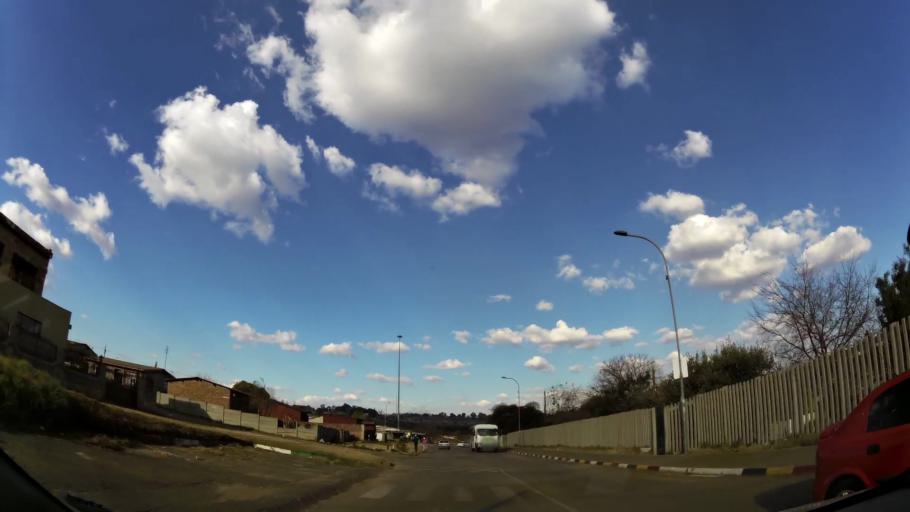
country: ZA
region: Mpumalanga
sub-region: Nkangala District Municipality
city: Witbank
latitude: -25.8740
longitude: 29.1876
